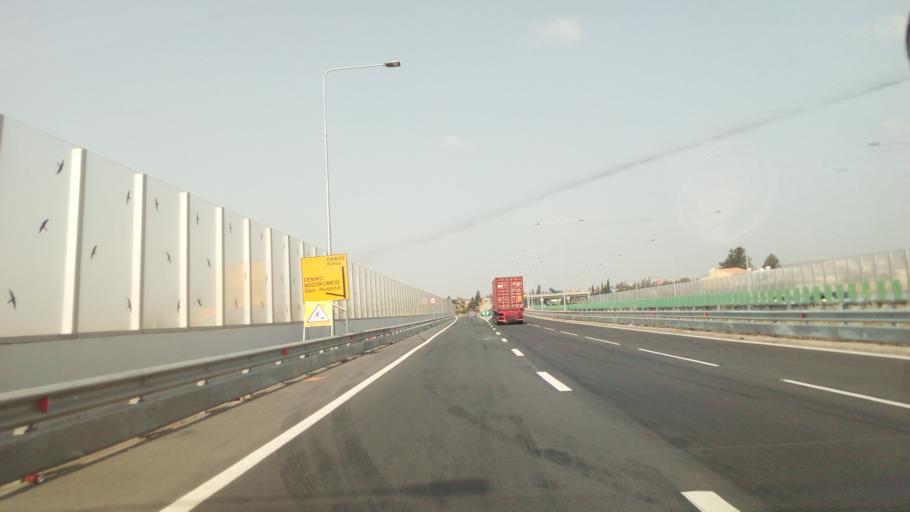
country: CY
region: Limassol
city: Pano Polemidia
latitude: 34.6869
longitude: 32.9953
